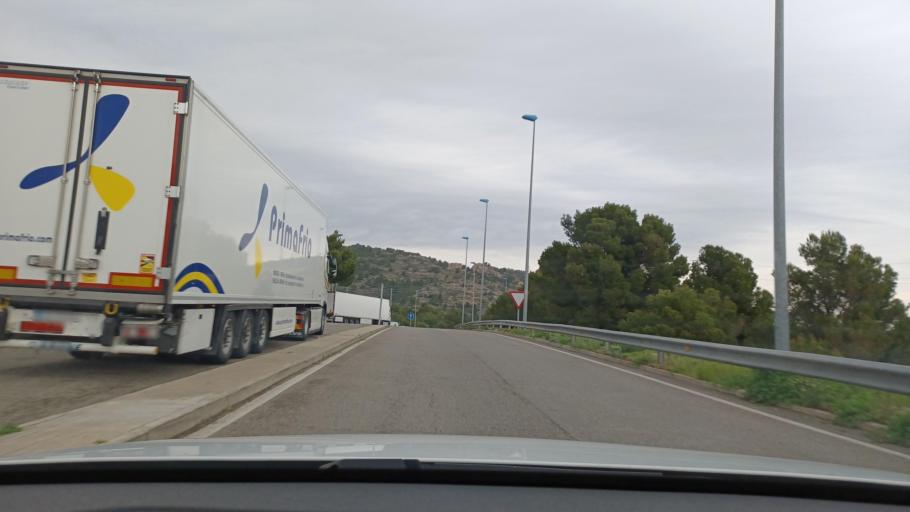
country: ES
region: Catalonia
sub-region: Provincia de Tarragona
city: Colldejou
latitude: 40.9857
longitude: 0.8975
